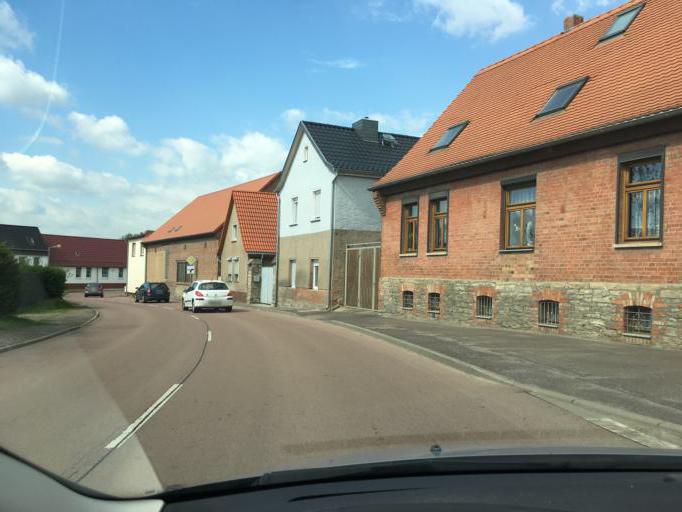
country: DE
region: Saxony-Anhalt
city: Belleben
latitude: 51.7172
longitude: 11.6149
